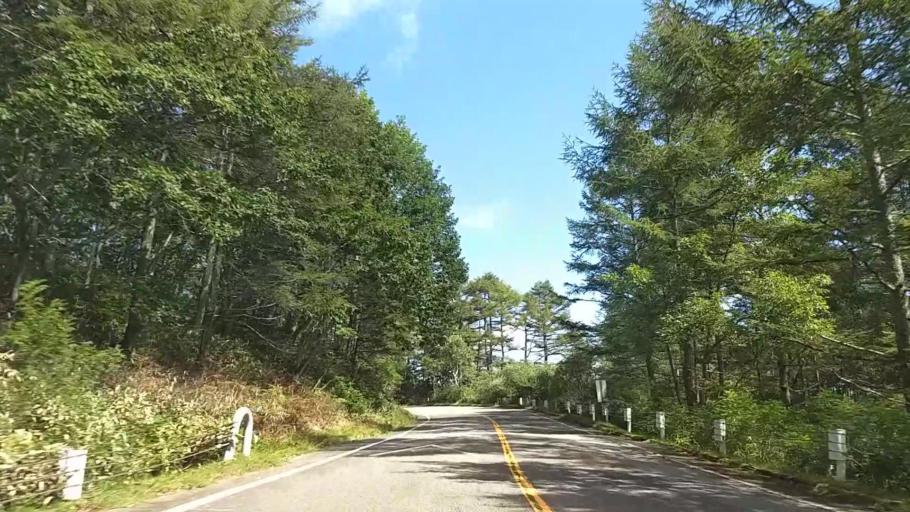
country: JP
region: Nagano
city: Suwa
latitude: 36.1530
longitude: 138.1409
